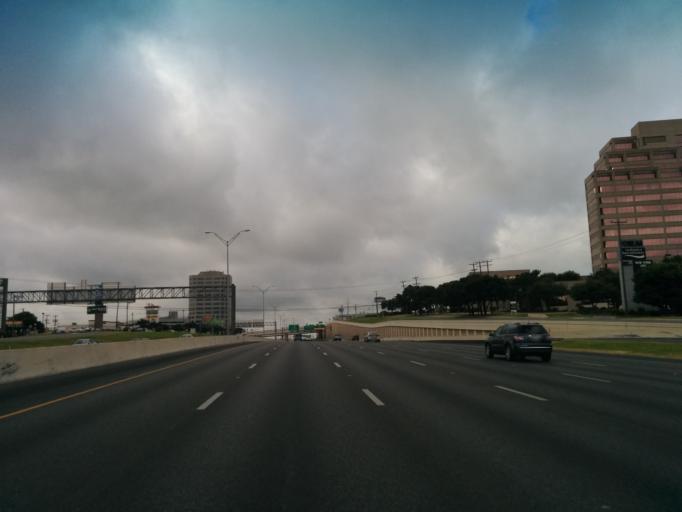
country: US
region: Texas
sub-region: Bexar County
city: Balcones Heights
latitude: 29.5159
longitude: -98.5538
